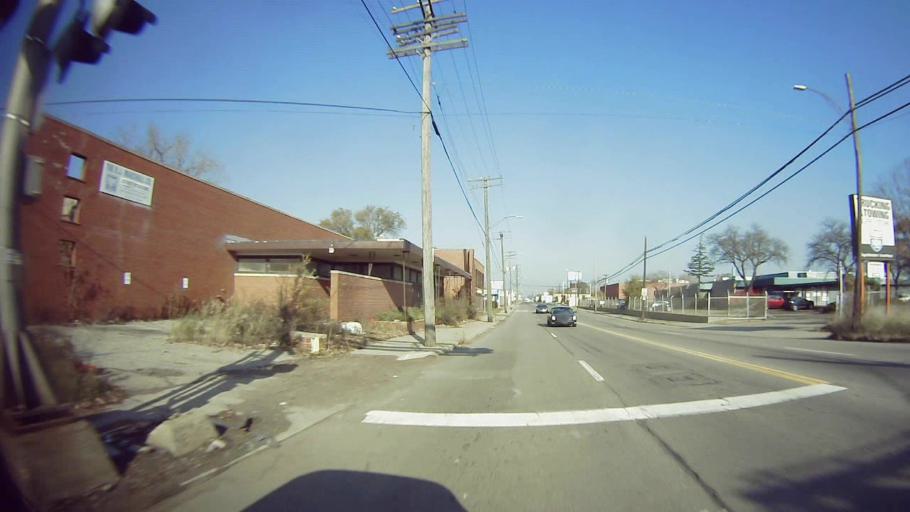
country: US
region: Michigan
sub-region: Oakland County
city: Oak Park
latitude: 42.3927
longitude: -83.1788
